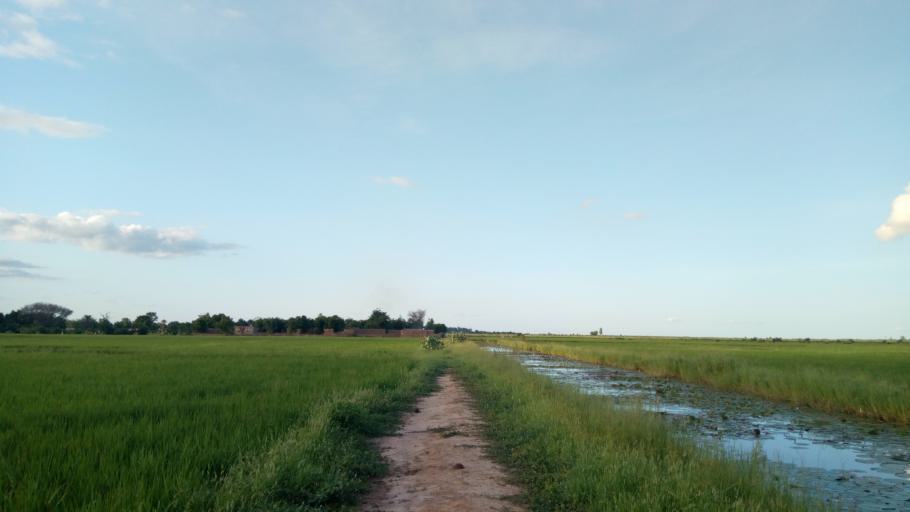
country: ML
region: Segou
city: Niono
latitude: 14.3082
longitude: -5.9536
